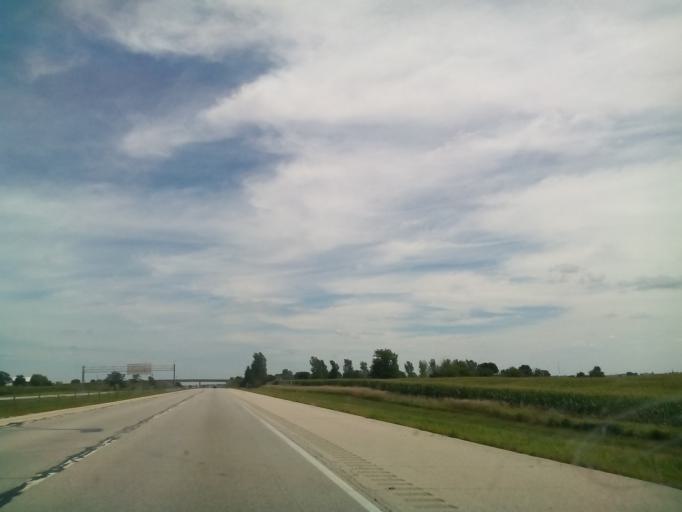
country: US
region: Illinois
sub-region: DeKalb County
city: Malta
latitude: 41.8997
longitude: -88.8548
